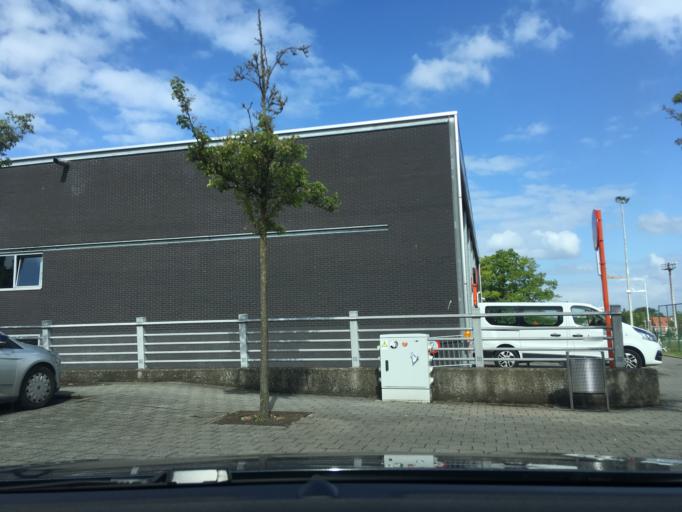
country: BE
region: Flanders
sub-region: Provincie West-Vlaanderen
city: Tielt
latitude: 51.0023
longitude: 3.3282
